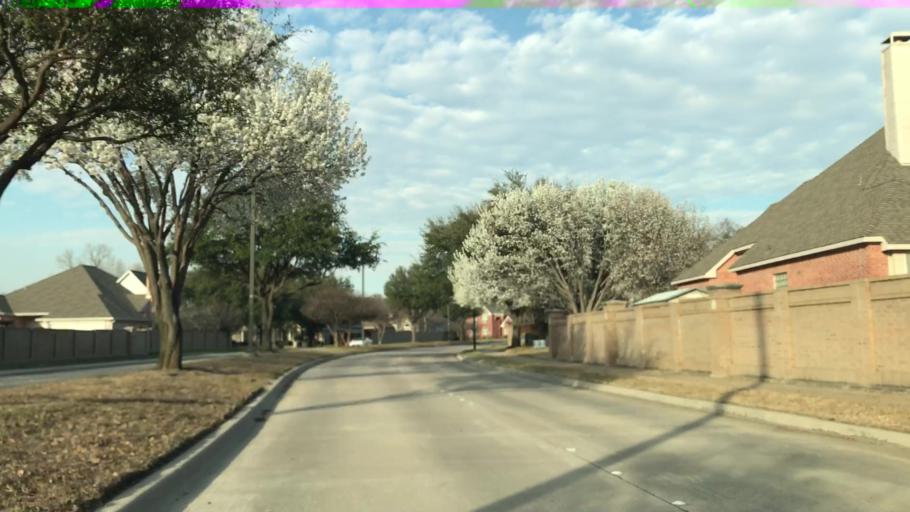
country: US
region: Texas
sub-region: Dallas County
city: Coppell
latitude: 32.9800
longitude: -97.0046
